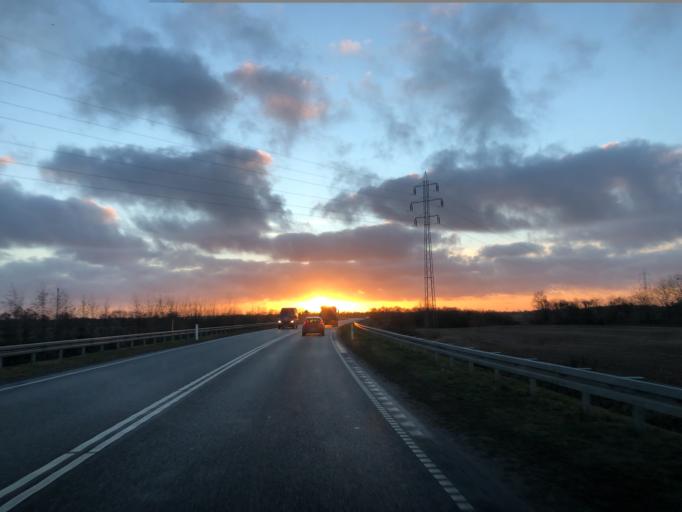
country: DK
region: Central Jutland
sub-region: Herning Kommune
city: Sunds
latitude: 56.2183
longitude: 9.0049
